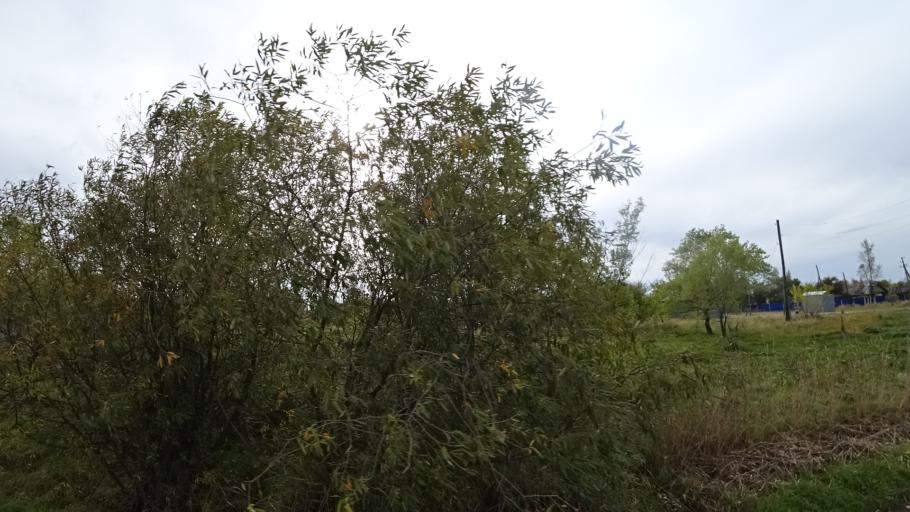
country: RU
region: Amur
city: Arkhara
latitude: 49.3088
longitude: 130.1792
